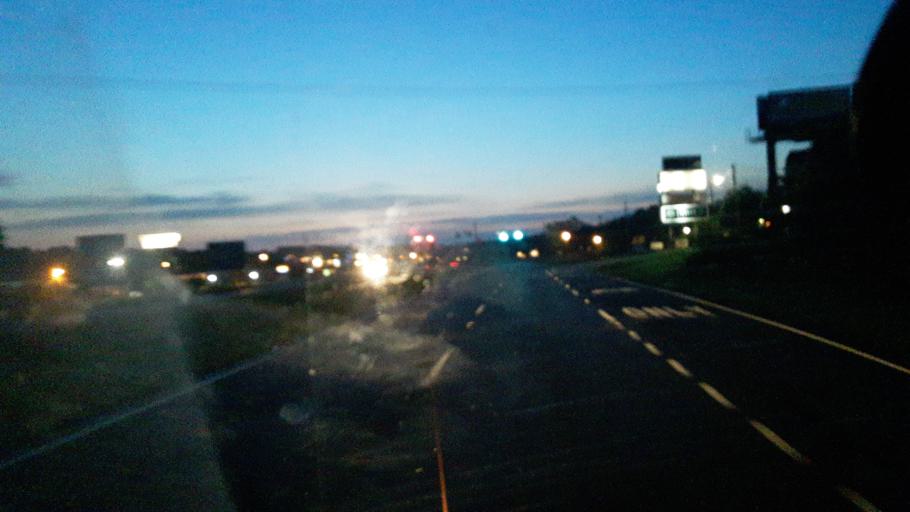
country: US
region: South Carolina
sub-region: Horry County
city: Little River
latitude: 33.8646
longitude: -78.6472
